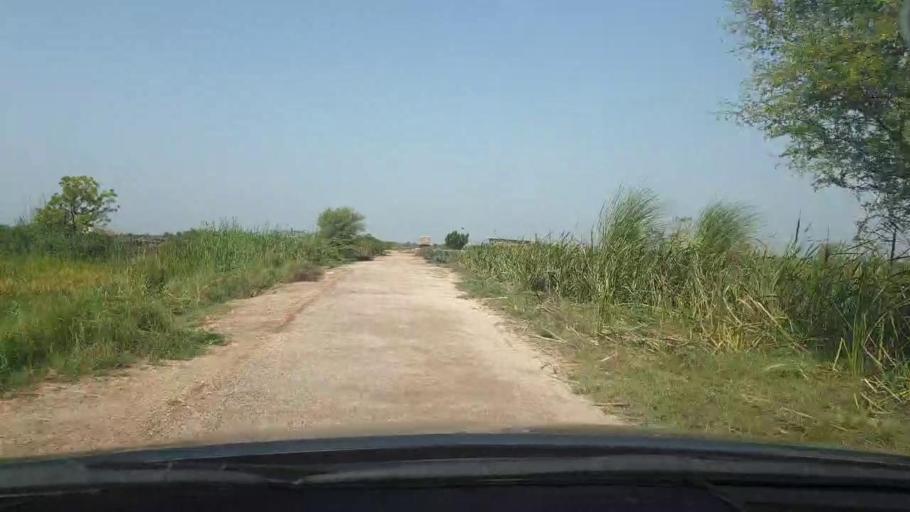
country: PK
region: Sindh
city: Tando Bago
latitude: 24.7092
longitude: 69.1128
